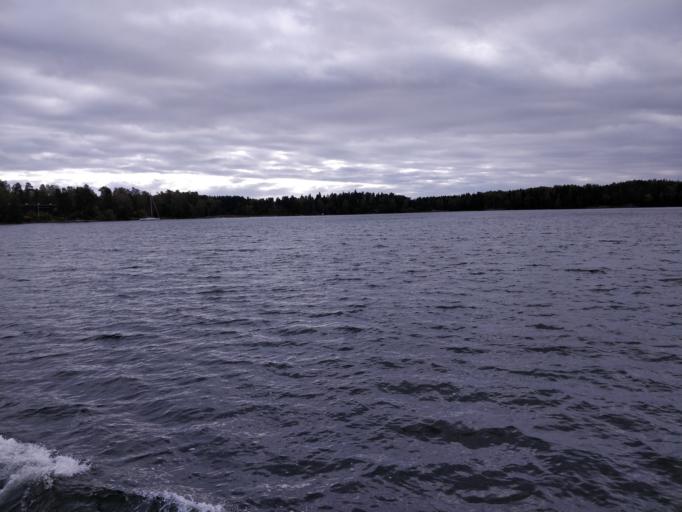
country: FI
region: Uusimaa
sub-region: Helsinki
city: Vantaa
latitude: 60.1755
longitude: 25.0785
